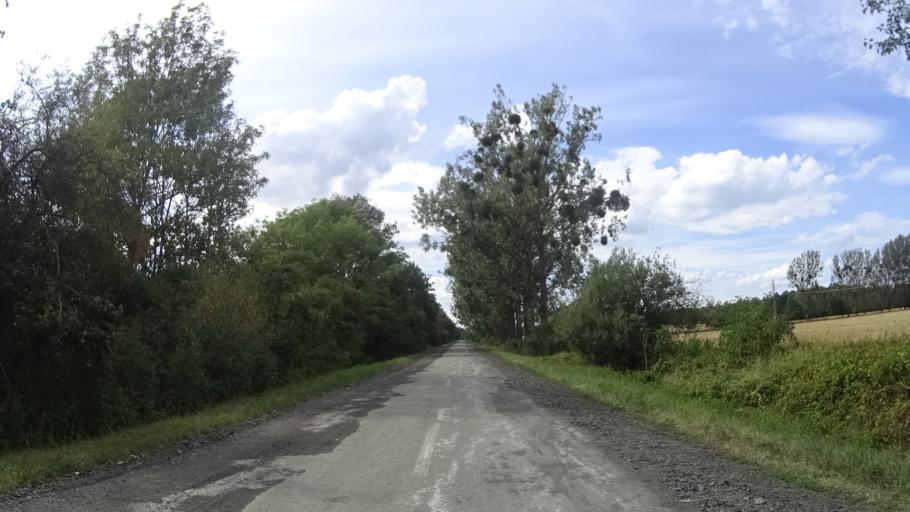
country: CZ
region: Olomoucky
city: Cervenka
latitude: 49.7157
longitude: 17.0494
